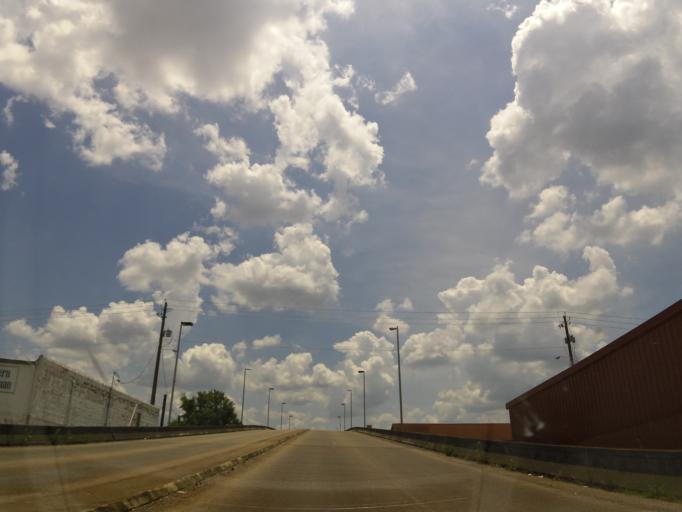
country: US
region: Mississippi
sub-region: Lauderdale County
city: Meridian
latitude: 32.3655
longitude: -88.6957
